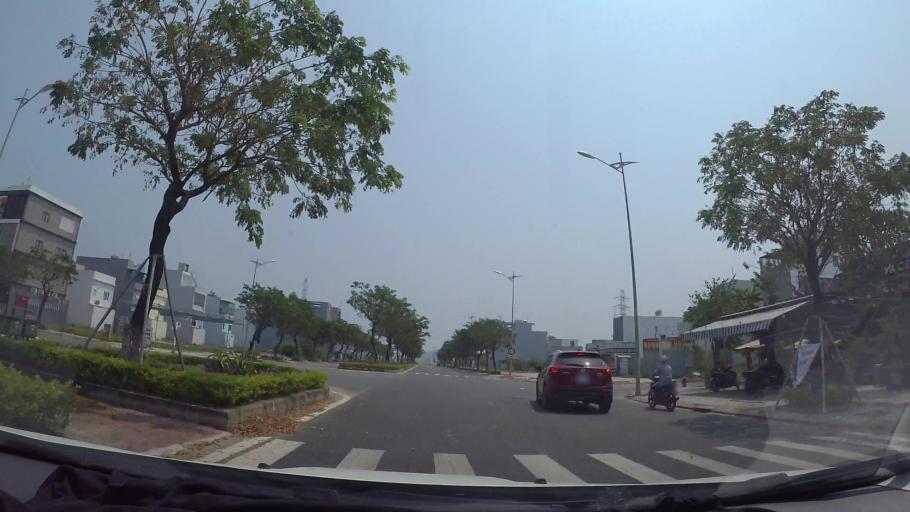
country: VN
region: Da Nang
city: Ngu Hanh Son
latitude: 16.0175
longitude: 108.2318
